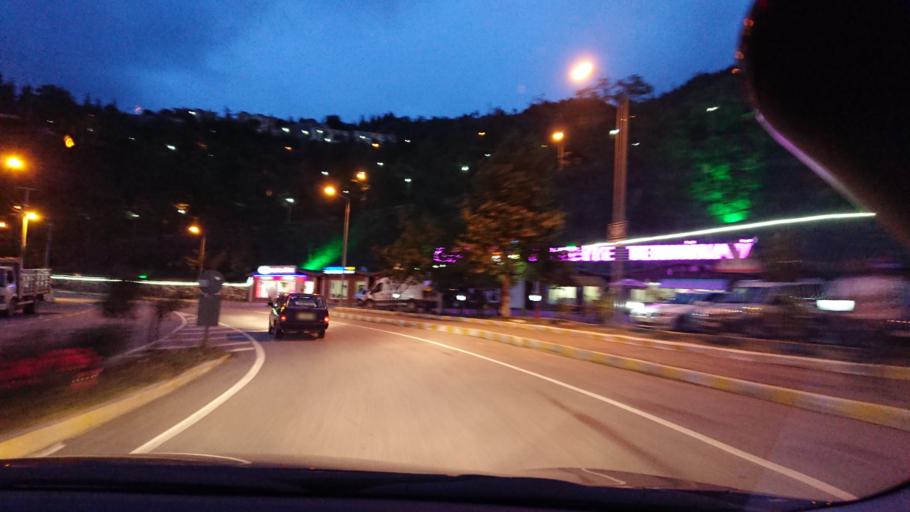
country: TR
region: Gumushane
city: Kurtun
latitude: 40.6706
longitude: 39.1401
